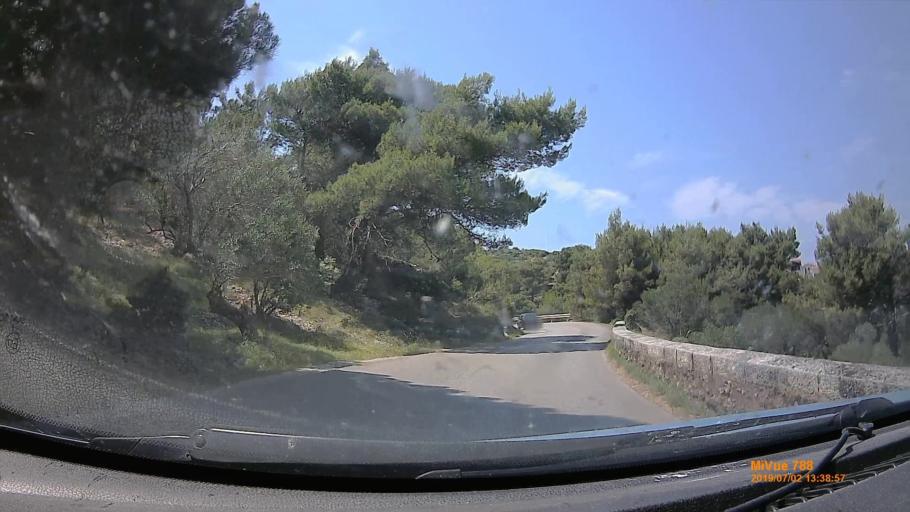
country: HR
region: Primorsko-Goranska
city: Mali Losinj
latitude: 44.5262
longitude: 14.4800
